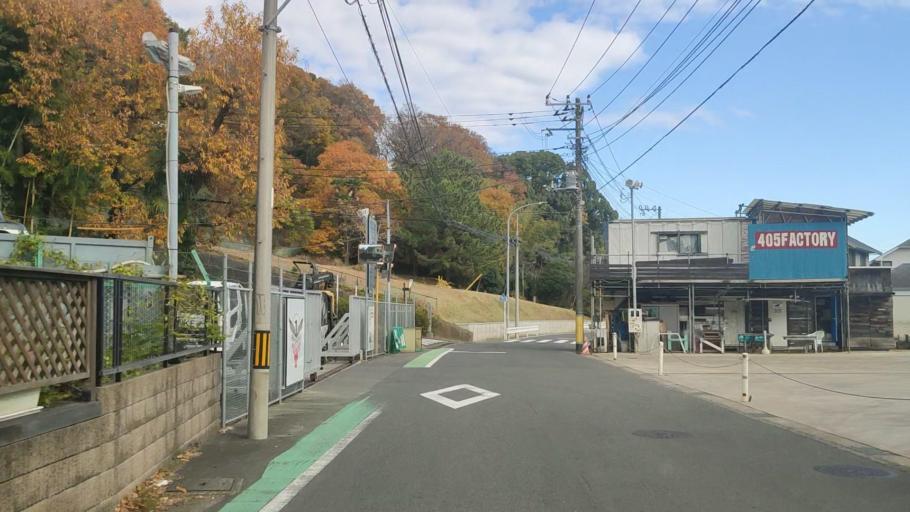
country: JP
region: Kanagawa
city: Yokohama
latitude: 35.4452
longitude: 139.5568
